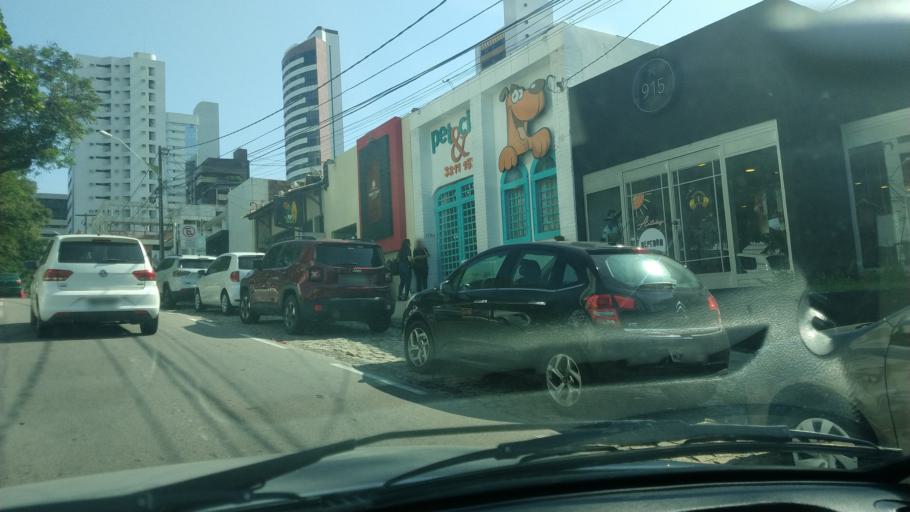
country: BR
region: Rio Grande do Norte
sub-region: Natal
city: Natal
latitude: -5.7990
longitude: -35.2013
